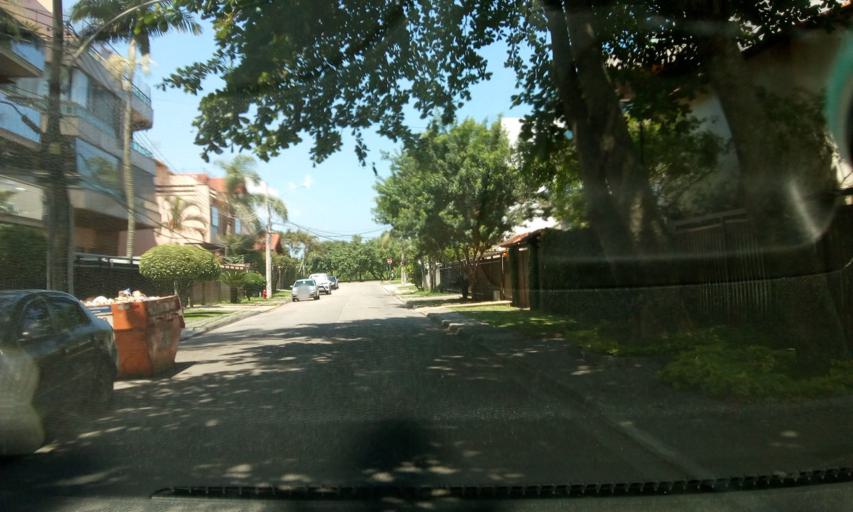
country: BR
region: Rio de Janeiro
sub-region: Nilopolis
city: Nilopolis
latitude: -23.0217
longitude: -43.4511
